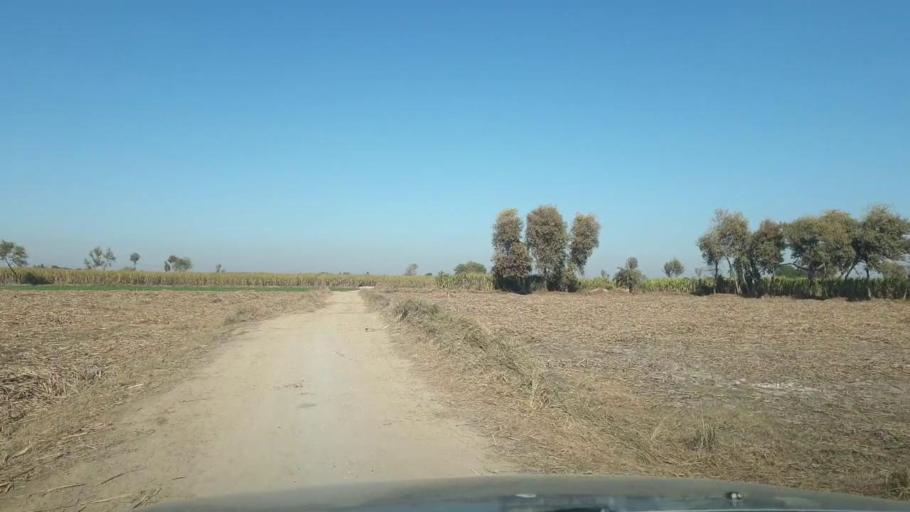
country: PK
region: Sindh
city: Ghotki
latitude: 28.0385
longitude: 69.2761
